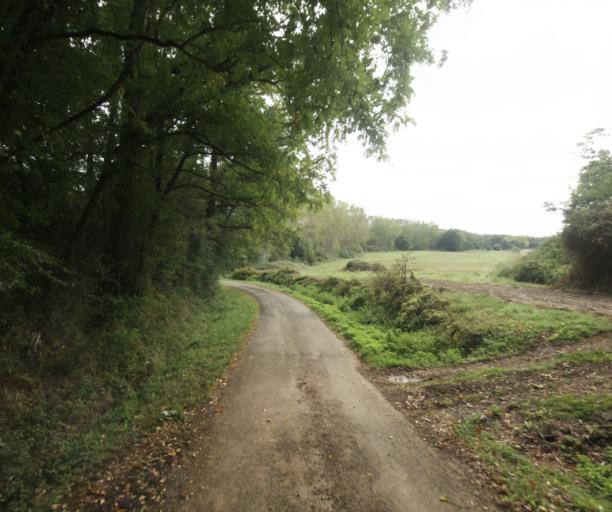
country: FR
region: Aquitaine
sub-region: Departement des Landes
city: Villeneuve-de-Marsan
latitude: 43.9083
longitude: -0.2318
